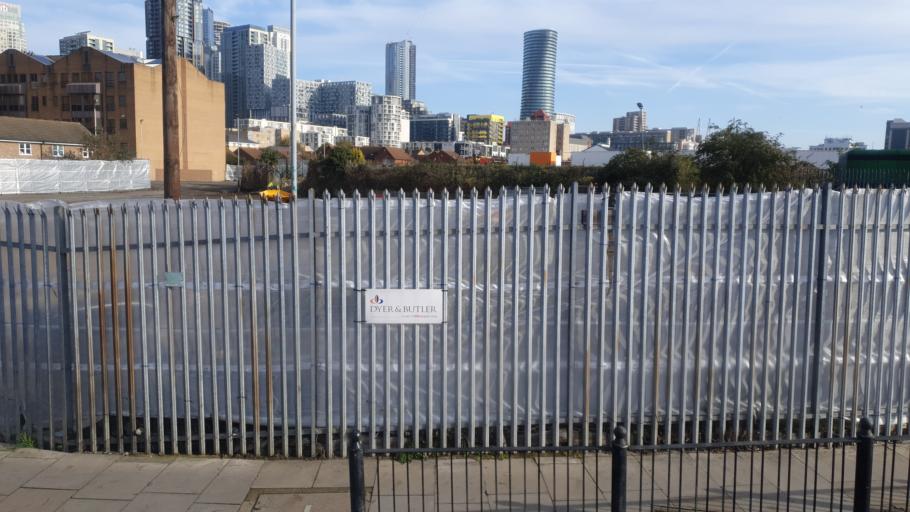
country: GB
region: England
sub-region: Greater London
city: Poplar
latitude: 51.4950
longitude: -0.0255
